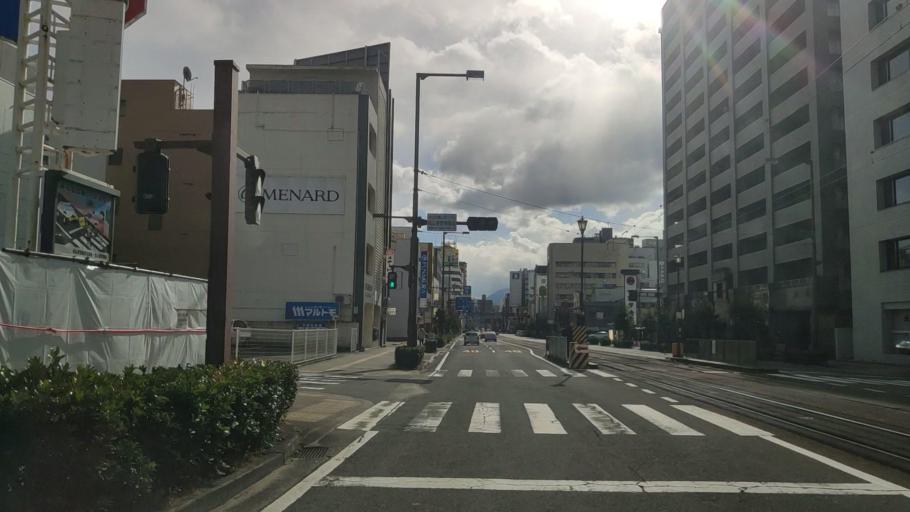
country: JP
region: Ehime
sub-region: Shikoku-chuo Shi
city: Matsuyama
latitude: 33.8446
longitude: 132.7754
